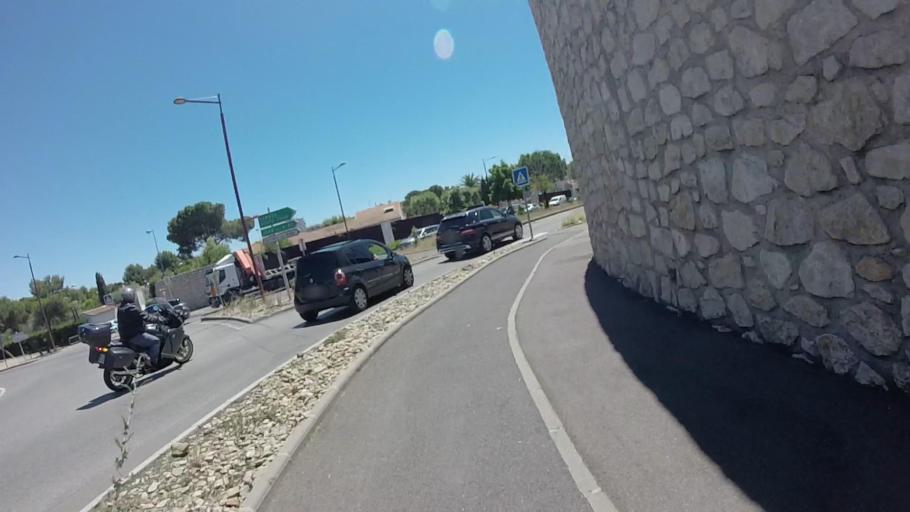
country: FR
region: Provence-Alpes-Cote d'Azur
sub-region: Departement des Alpes-Maritimes
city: Biot
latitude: 43.5959
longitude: 7.0901
